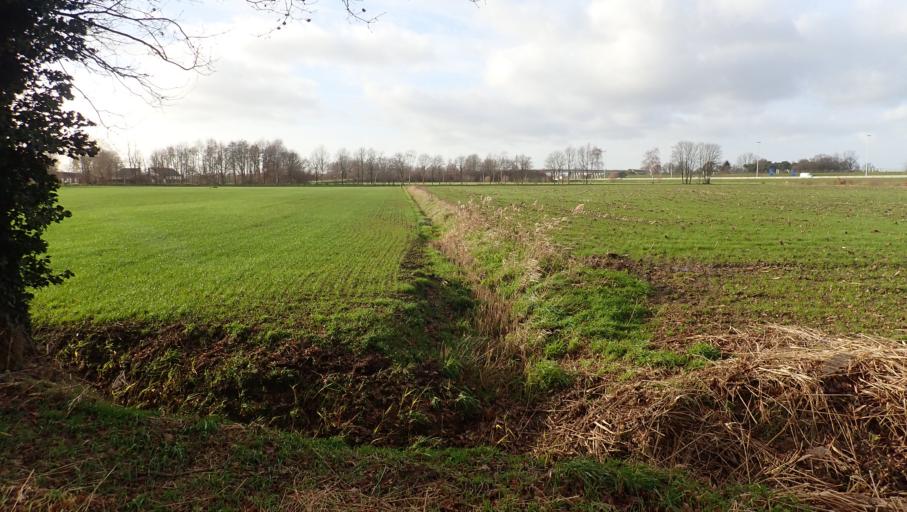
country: BE
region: Flanders
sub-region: Provincie Antwerpen
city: Brecht
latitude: 51.3697
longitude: 4.6550
